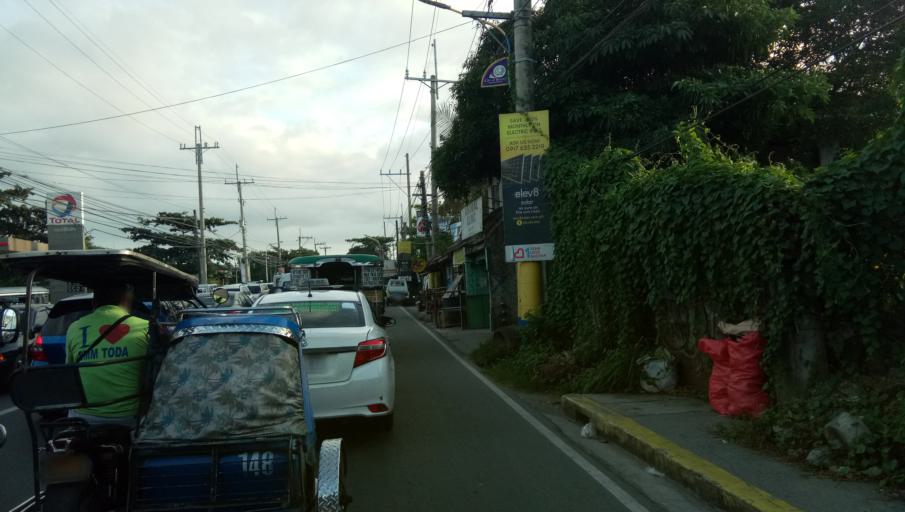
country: PH
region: Calabarzon
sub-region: Province of Cavite
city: Imus
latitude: 14.3819
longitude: 120.9785
